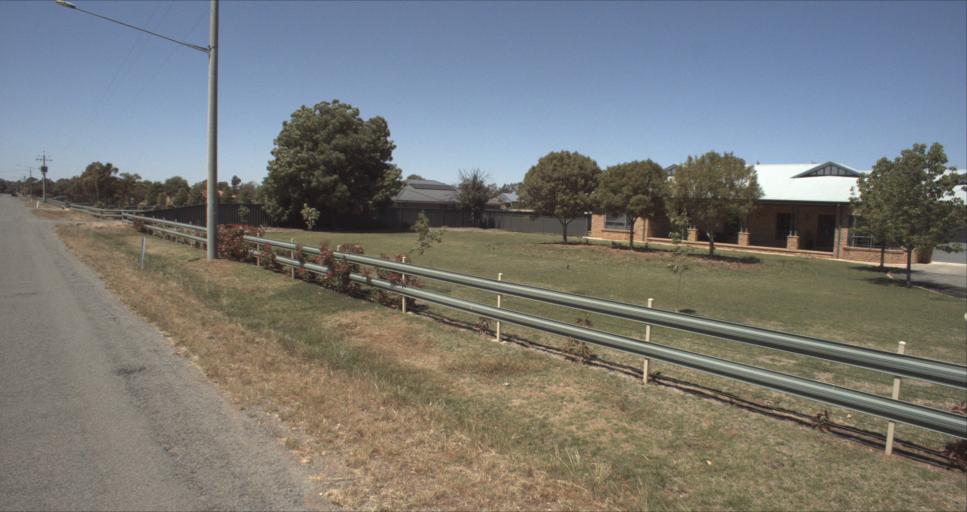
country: AU
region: New South Wales
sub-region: Leeton
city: Leeton
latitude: -34.5275
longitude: 146.3954
